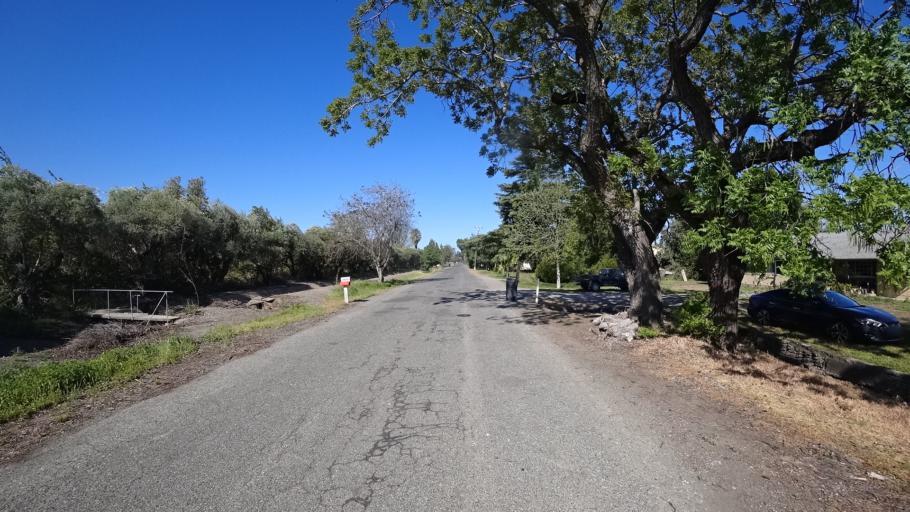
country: US
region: California
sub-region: Glenn County
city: Orland
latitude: 39.7289
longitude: -122.1573
